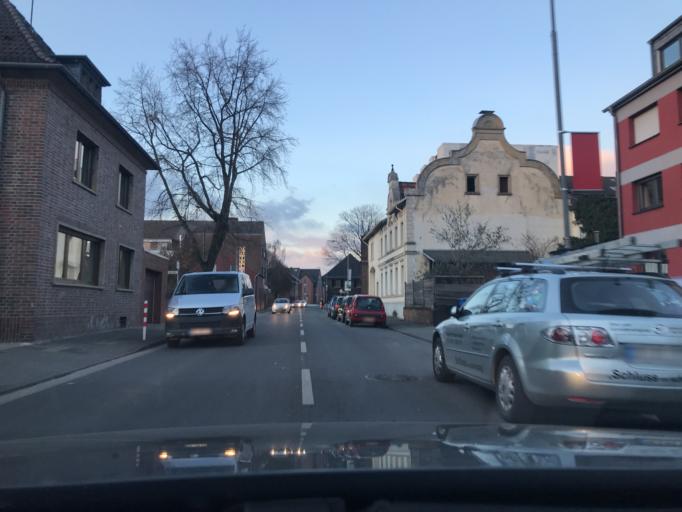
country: DE
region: North Rhine-Westphalia
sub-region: Regierungsbezirk Dusseldorf
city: Kaarst
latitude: 51.2330
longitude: 6.6180
